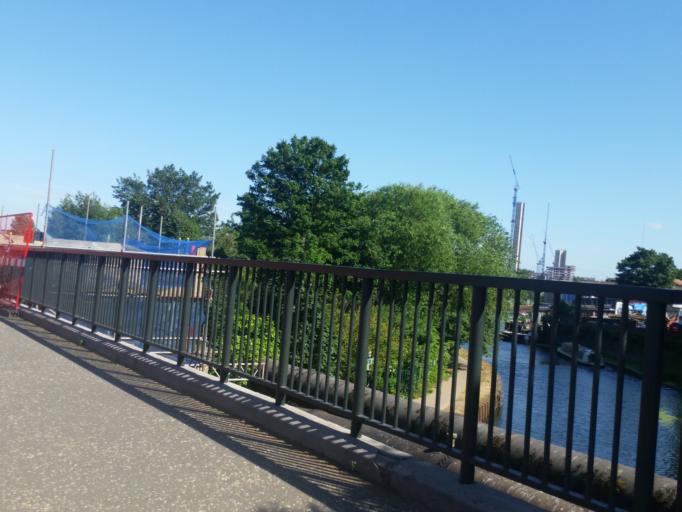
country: GB
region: England
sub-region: Greater London
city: Poplar
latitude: 51.5367
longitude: -0.0213
